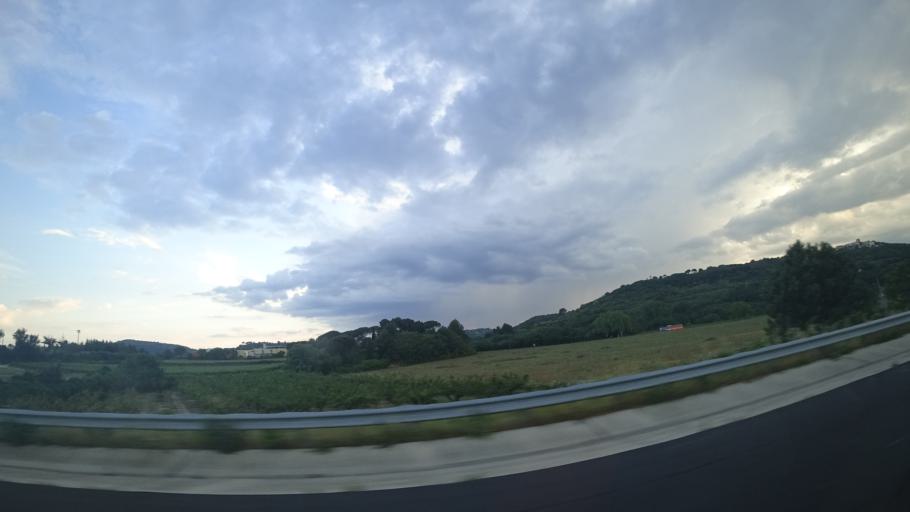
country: FR
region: Languedoc-Roussillon
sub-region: Departement de l'Herault
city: Nebian
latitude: 43.6387
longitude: 3.4463
